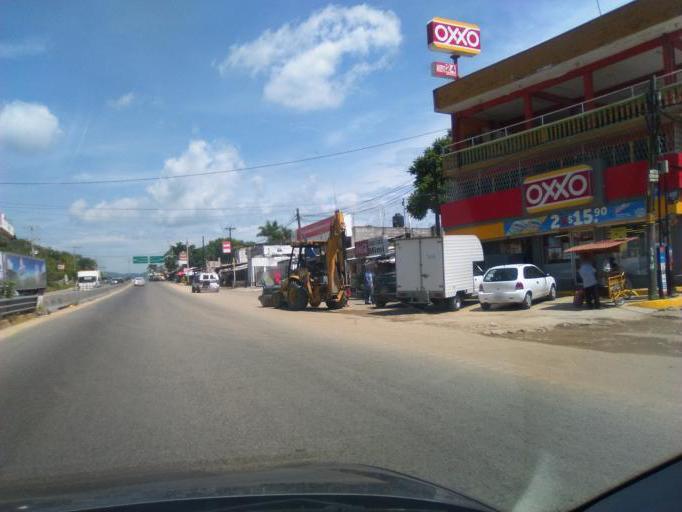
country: MX
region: Guerrero
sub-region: Acapulco de Juarez
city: Colonia Nueva Revolucion
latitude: 16.9170
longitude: -99.8191
